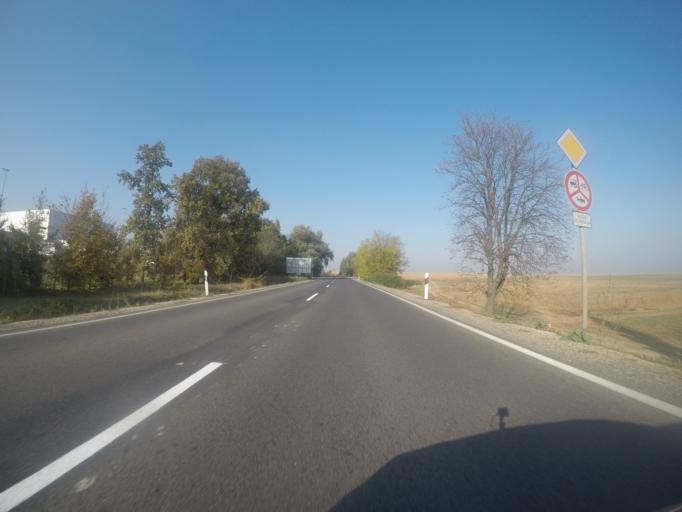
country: HU
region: Fejer
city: Racalmas
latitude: 47.0014
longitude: 18.9307
